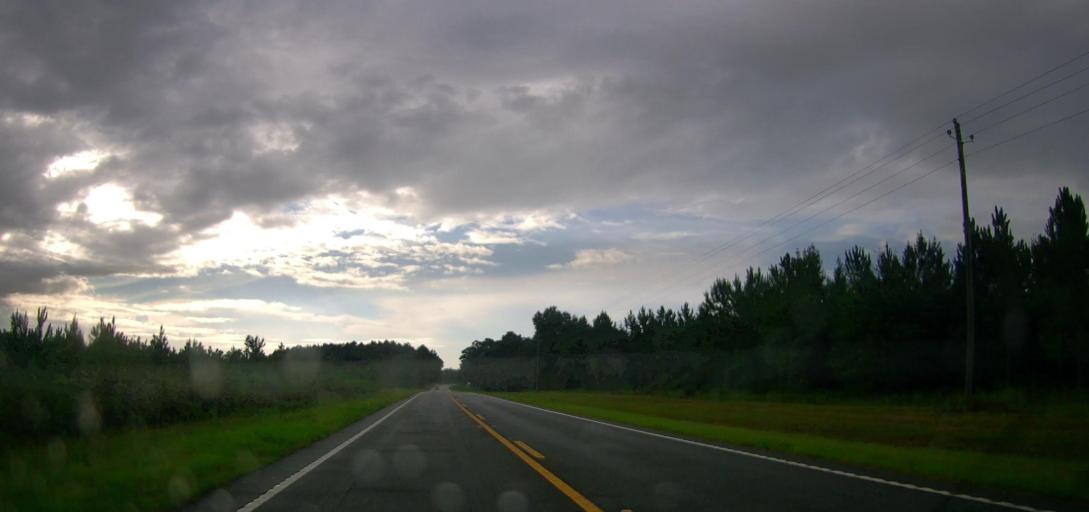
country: US
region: Georgia
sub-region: Ware County
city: Deenwood
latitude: 31.2805
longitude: -82.5407
